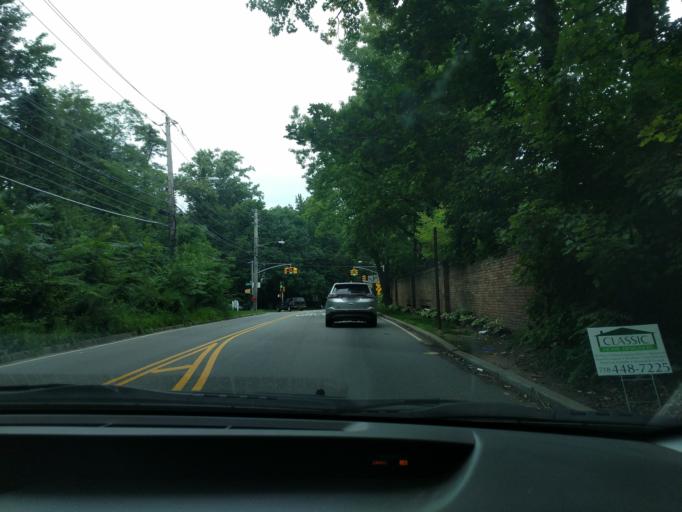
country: US
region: New York
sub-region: Richmond County
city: Staten Island
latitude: 40.6016
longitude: -74.1144
